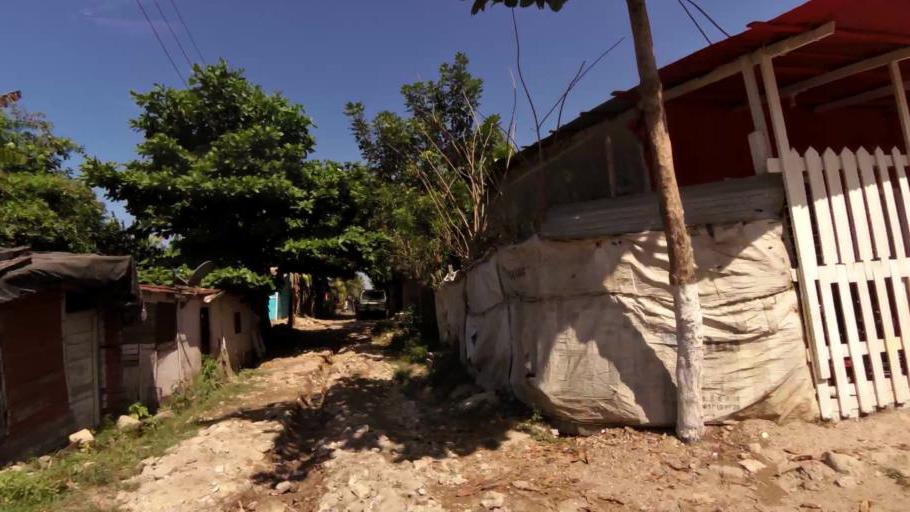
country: CO
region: Bolivar
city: Cartagena
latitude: 10.3666
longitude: -75.4942
